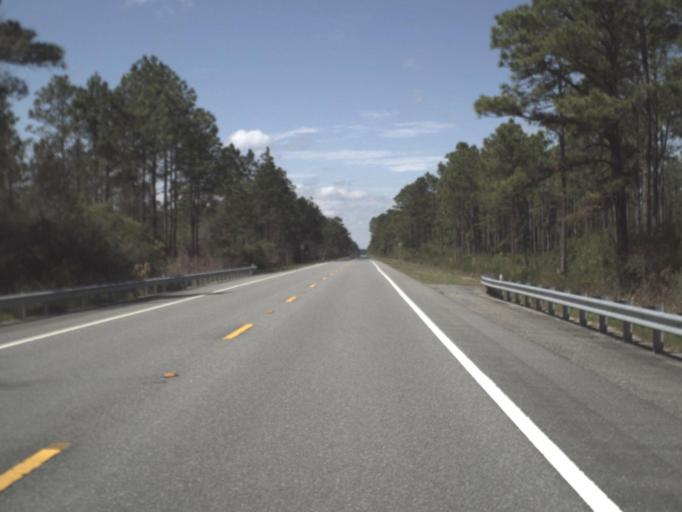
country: US
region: Florida
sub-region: Gadsden County
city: Midway
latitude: 30.3424
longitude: -84.4952
